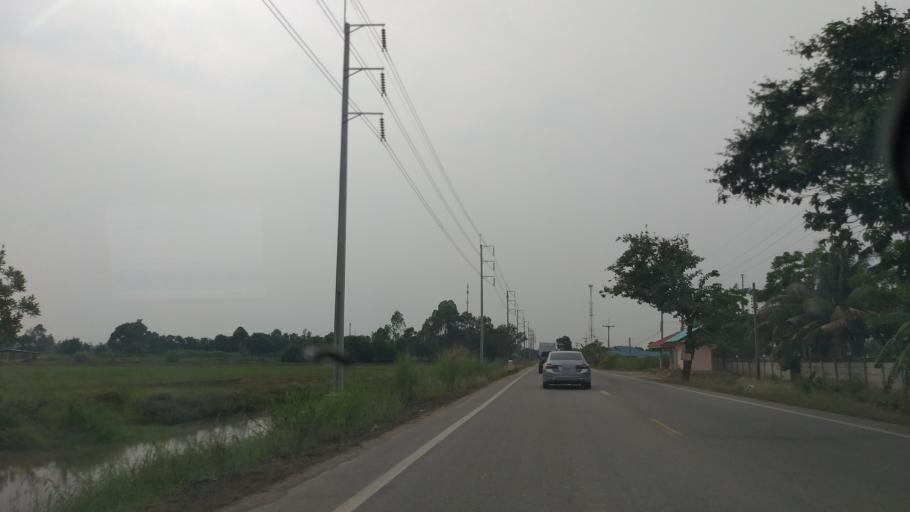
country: TH
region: Chachoengsao
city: Plaeng Yao
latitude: 13.5959
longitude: 101.1894
